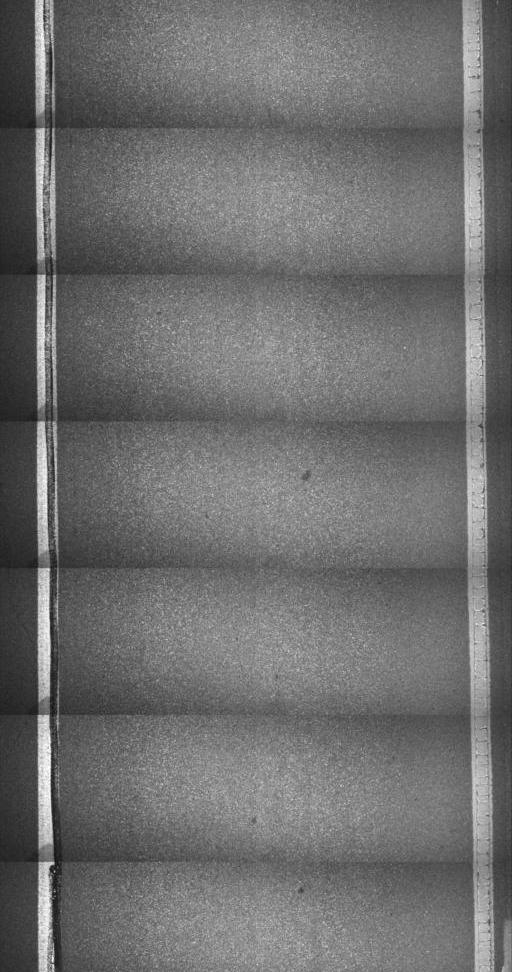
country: US
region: Vermont
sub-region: Rutland County
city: West Rutland
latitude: 43.6311
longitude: -73.0339
